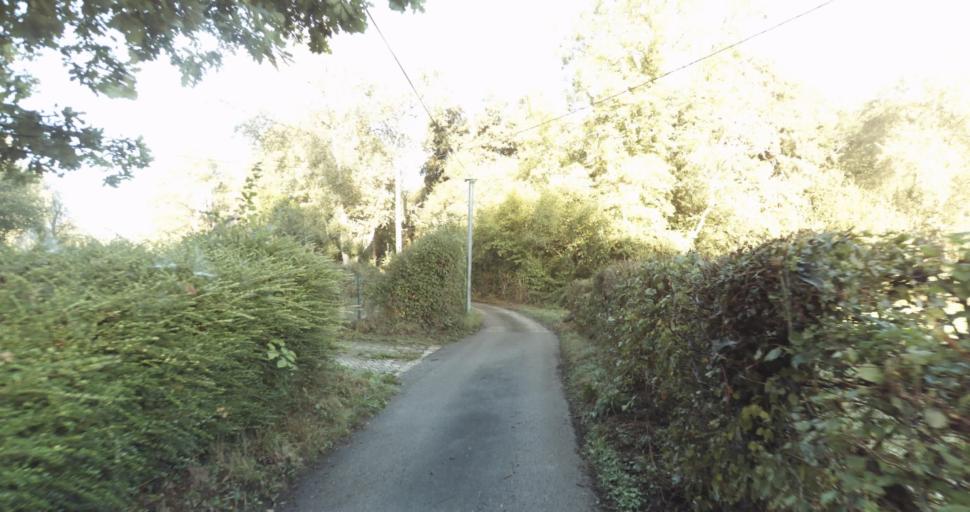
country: FR
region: Lower Normandy
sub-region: Departement de l'Orne
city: Vimoutiers
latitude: 48.9225
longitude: 0.1760
